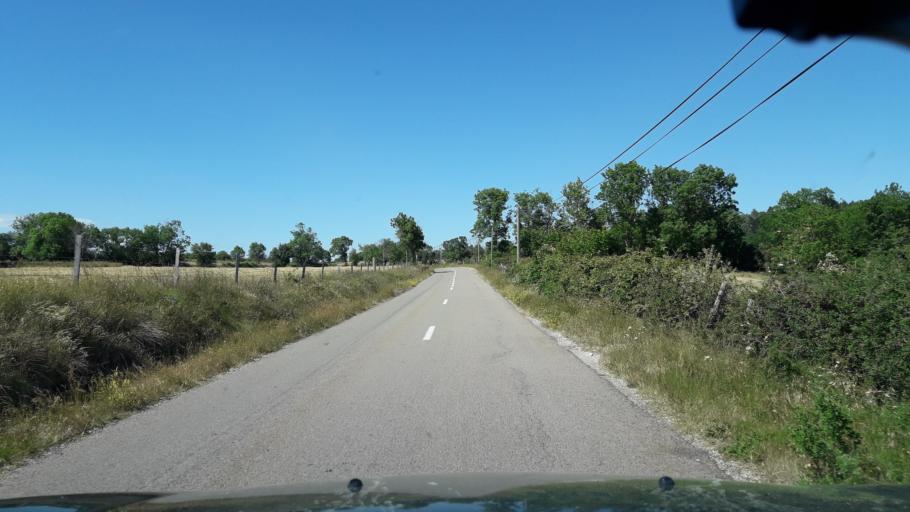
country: FR
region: Rhone-Alpes
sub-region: Departement de l'Ardeche
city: Saint-Priest
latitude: 44.6474
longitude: 4.5612
